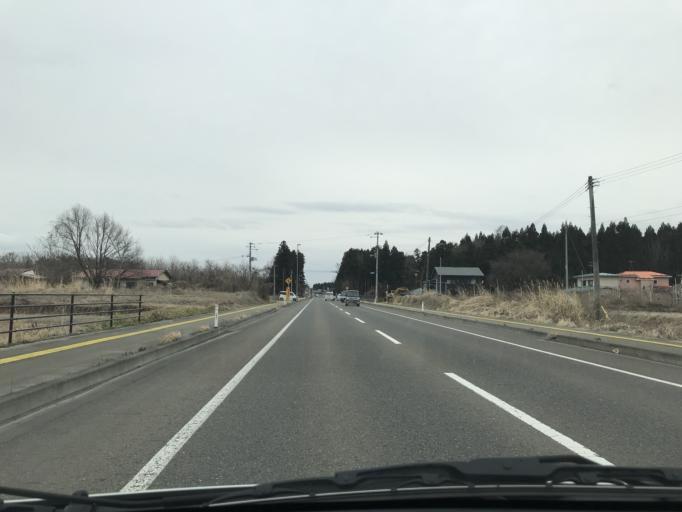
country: JP
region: Iwate
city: Hanamaki
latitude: 39.3655
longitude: 141.1111
